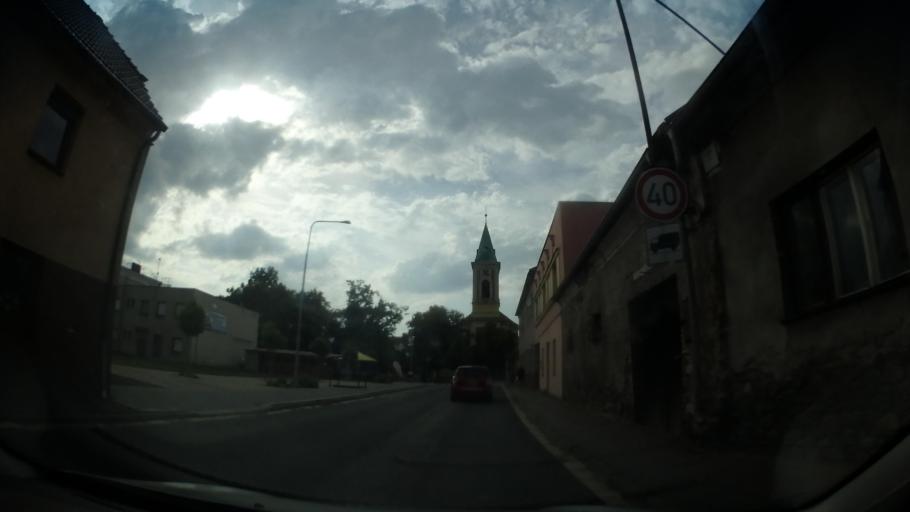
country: CZ
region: Pardubicky
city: Ronov nad Doubravou
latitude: 49.8882
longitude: 15.5323
